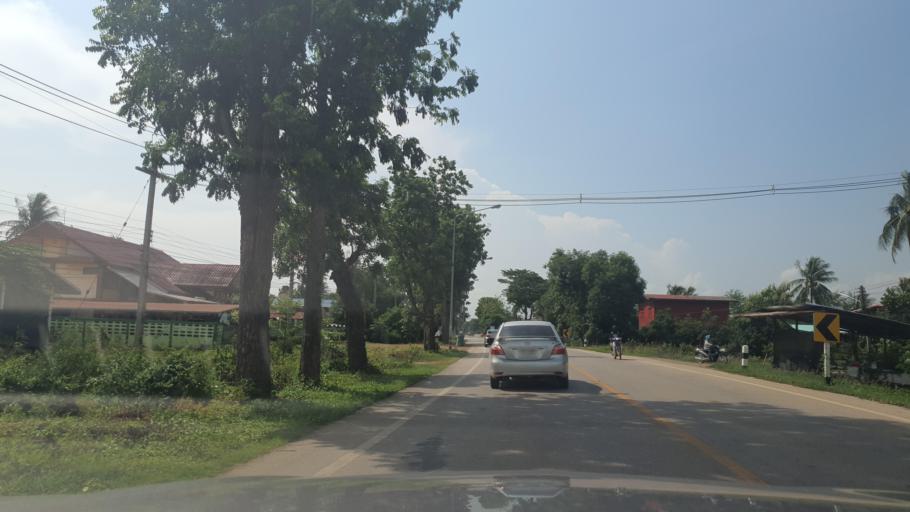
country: TH
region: Sukhothai
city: Si Samrong
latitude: 17.1928
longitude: 99.8507
